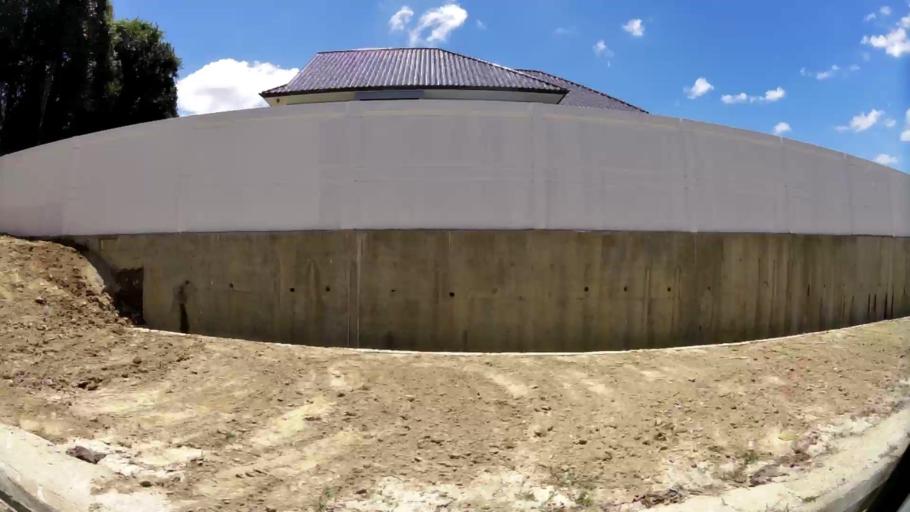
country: BN
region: Brunei and Muara
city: Bandar Seri Begawan
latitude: 4.9415
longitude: 114.9620
